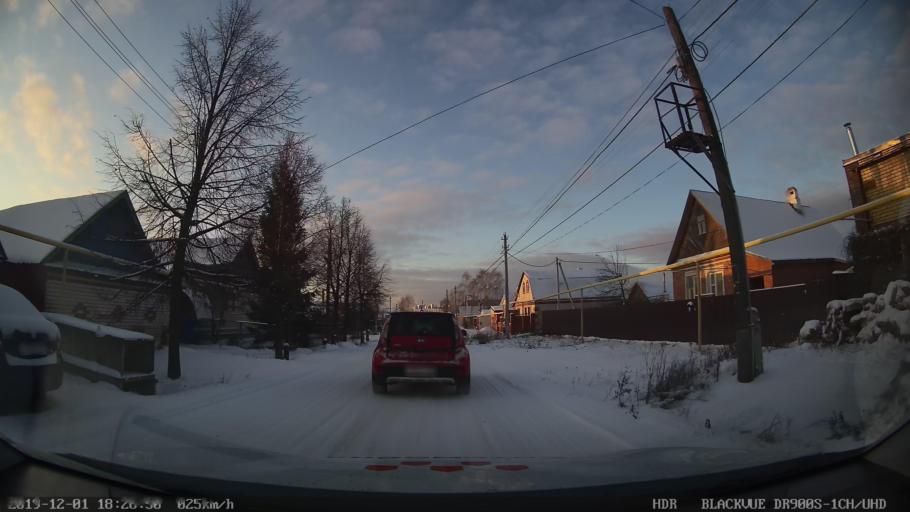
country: RU
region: Tatarstan
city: Vysokaya Gora
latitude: 55.8063
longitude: 49.2557
